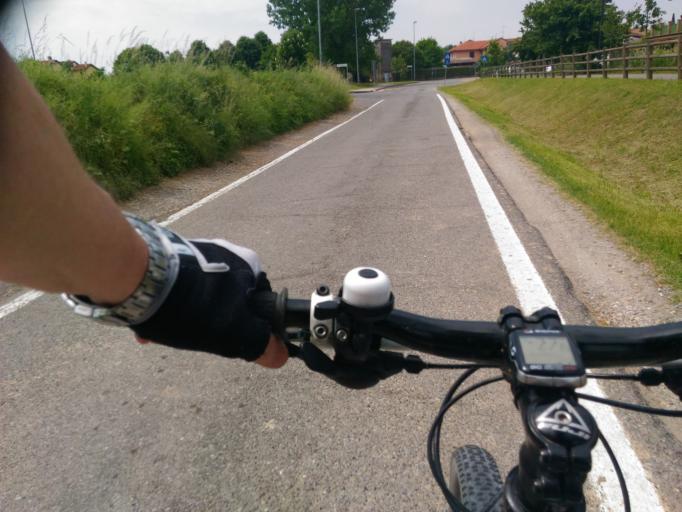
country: IT
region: Lombardy
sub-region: Provincia di Lodi
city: Tavazzano
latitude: 45.3372
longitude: 9.4086
